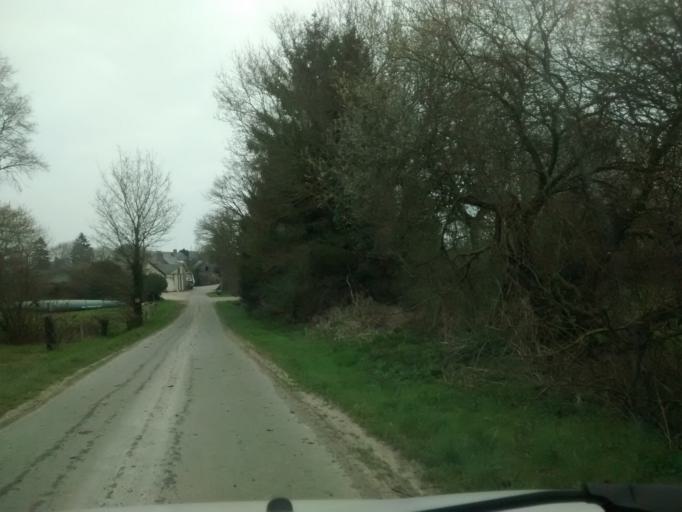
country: FR
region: Brittany
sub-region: Departement d'Ille-et-Vilaine
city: Bazouges-la-Perouse
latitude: 48.4003
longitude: -1.5803
